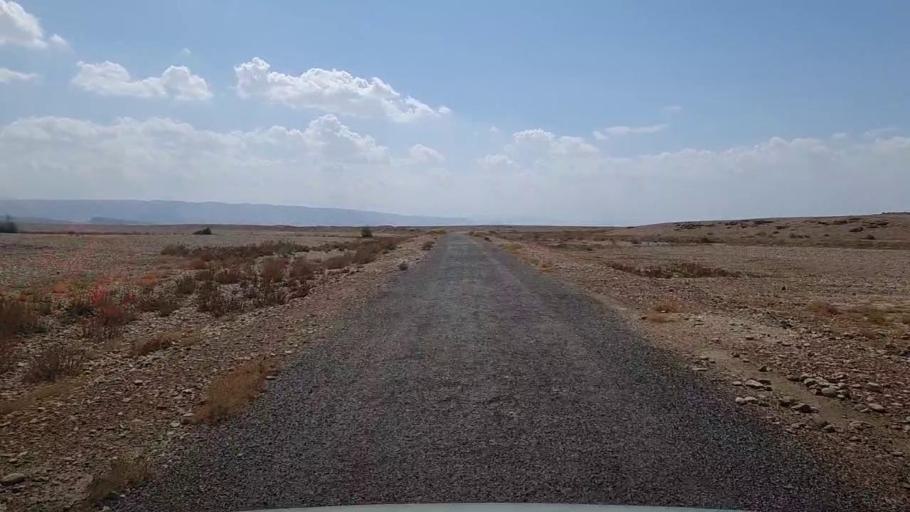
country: PK
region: Sindh
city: Bhan
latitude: 26.3812
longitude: 67.6311
